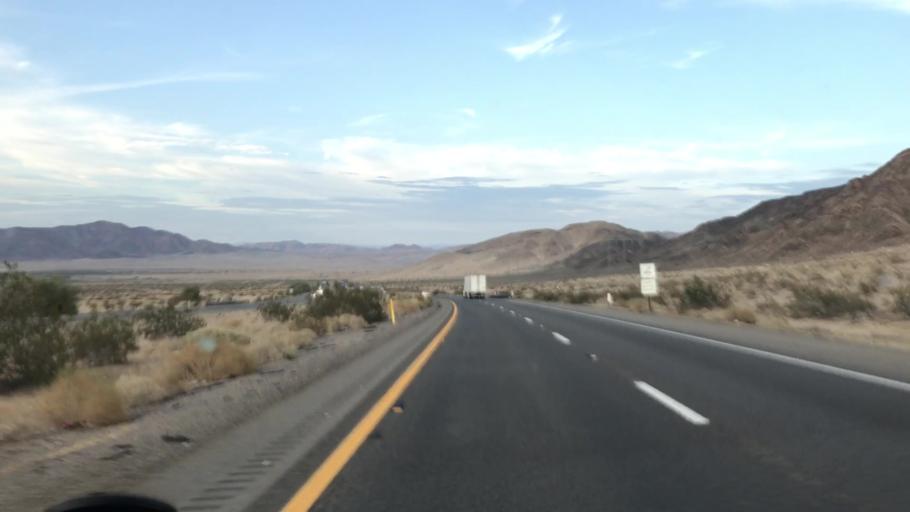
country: US
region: California
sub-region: San Bernardino County
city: Fort Irwin
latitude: 35.0873
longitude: -116.3194
